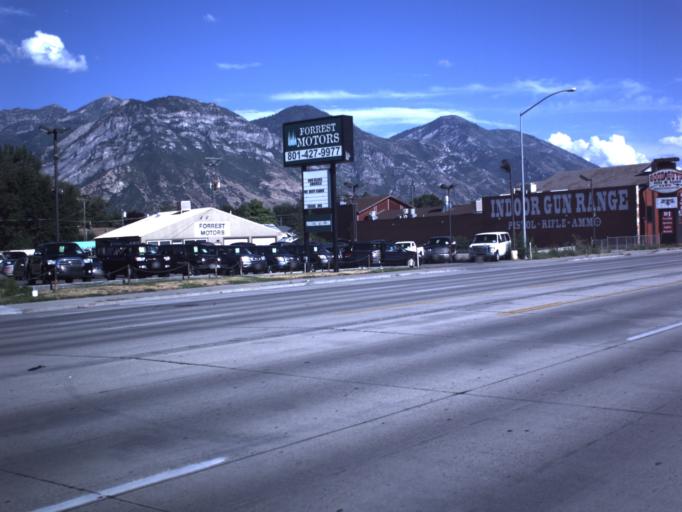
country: US
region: Utah
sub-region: Utah County
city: Orem
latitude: 40.2805
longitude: -111.6879
